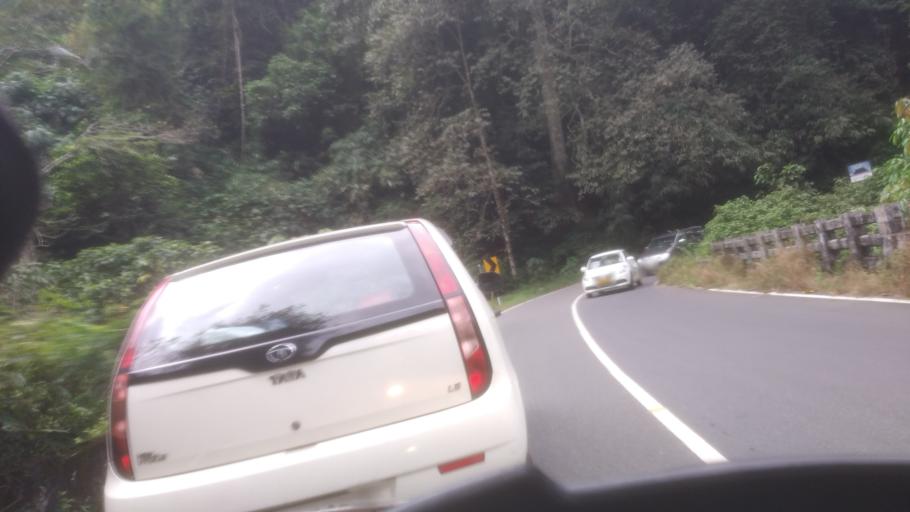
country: IN
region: Kerala
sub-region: Idukki
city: Kuttampuzha
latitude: 10.0655
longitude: 76.8068
